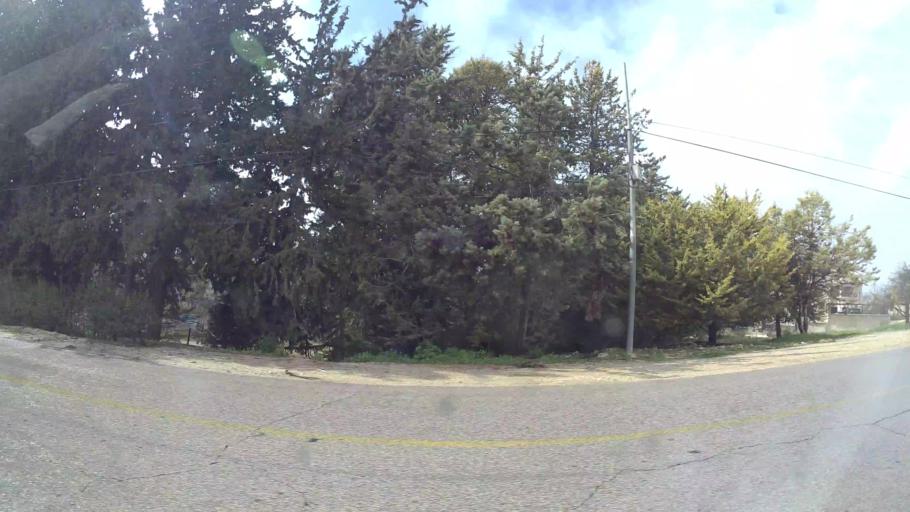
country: JO
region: Amman
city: Al Jubayhah
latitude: 32.0260
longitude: 35.8211
